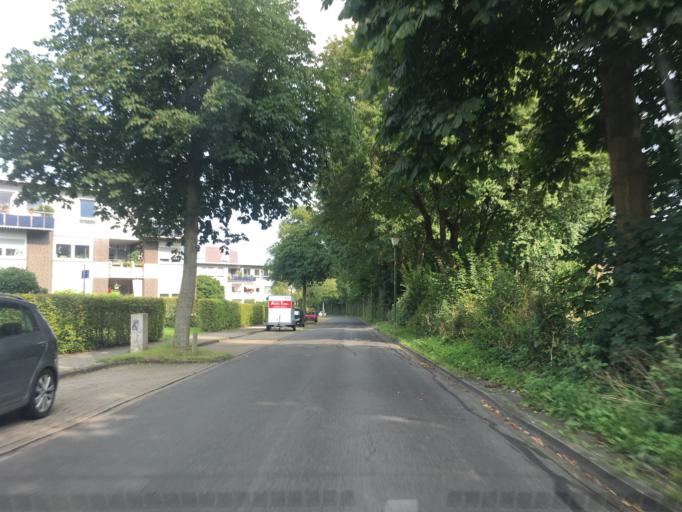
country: DE
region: North Rhine-Westphalia
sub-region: Regierungsbezirk Munster
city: Muenster
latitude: 51.9834
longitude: 7.6423
